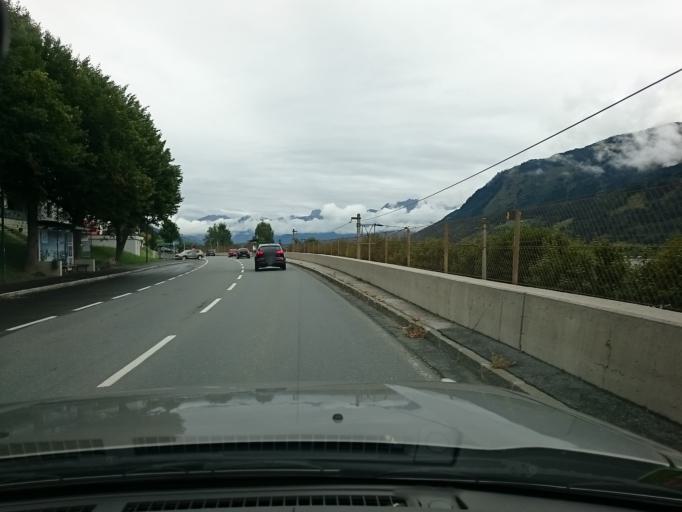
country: AT
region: Salzburg
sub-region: Politischer Bezirk Zell am See
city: Zell am See
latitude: 47.3341
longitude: 12.7975
